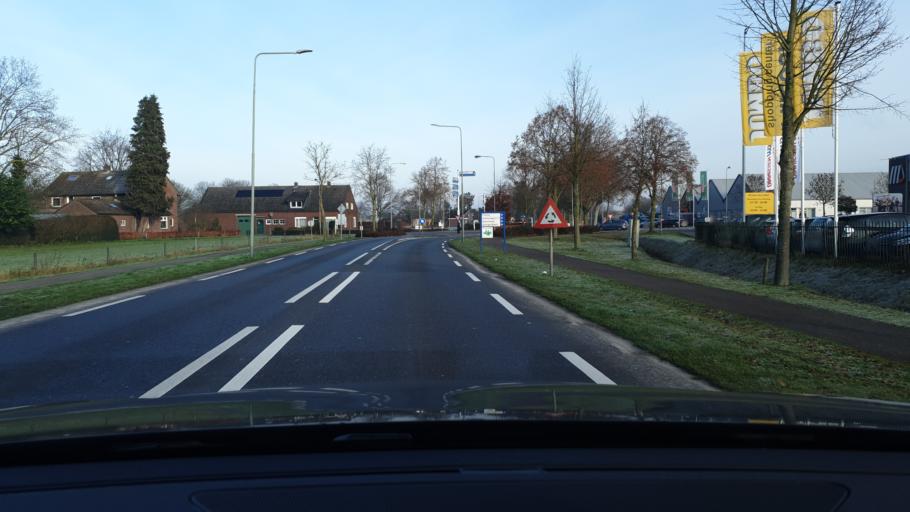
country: NL
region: Limburg
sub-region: Gemeente Peel en Maas
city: Maasbree
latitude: 51.4243
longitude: 6.0352
